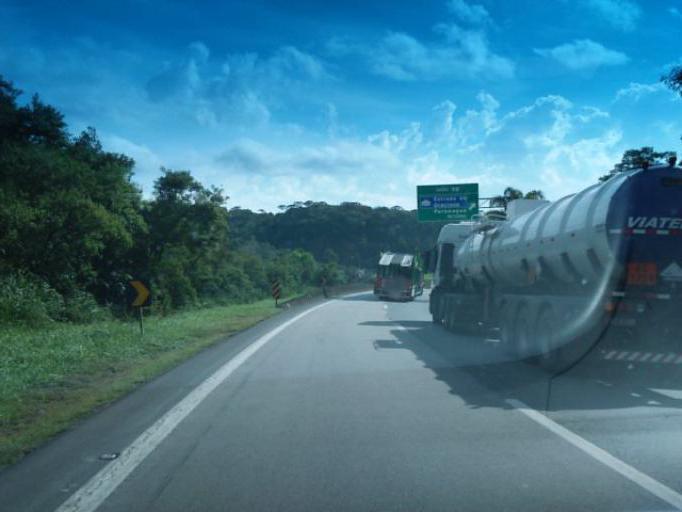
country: BR
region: Parana
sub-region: Campina Grande Do Sul
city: Campina Grande do Sul
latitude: -25.3028
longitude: -48.9432
